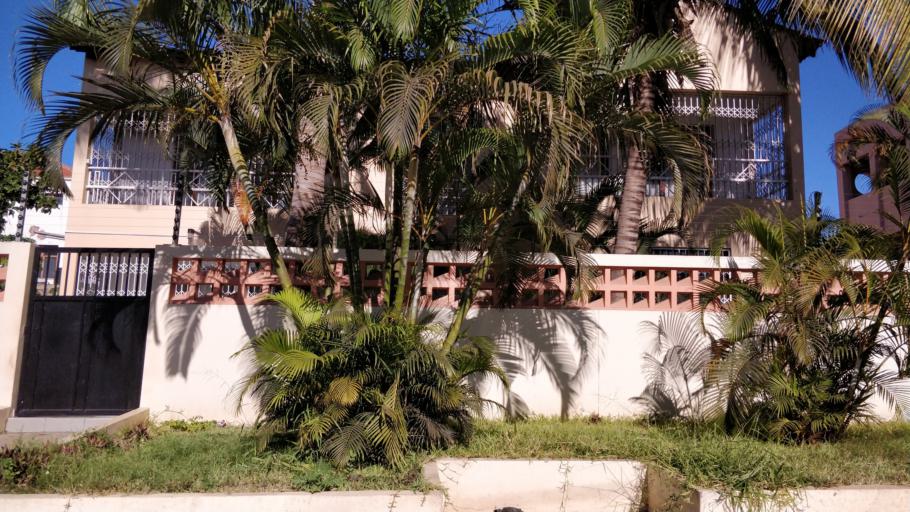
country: MZ
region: Maputo City
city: Maputo
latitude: -25.9453
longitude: 32.6132
